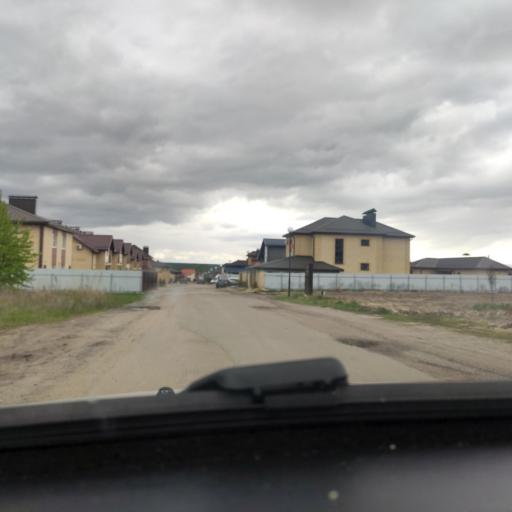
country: RU
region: Voronezj
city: Podgornoye
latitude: 51.7552
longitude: 39.1481
